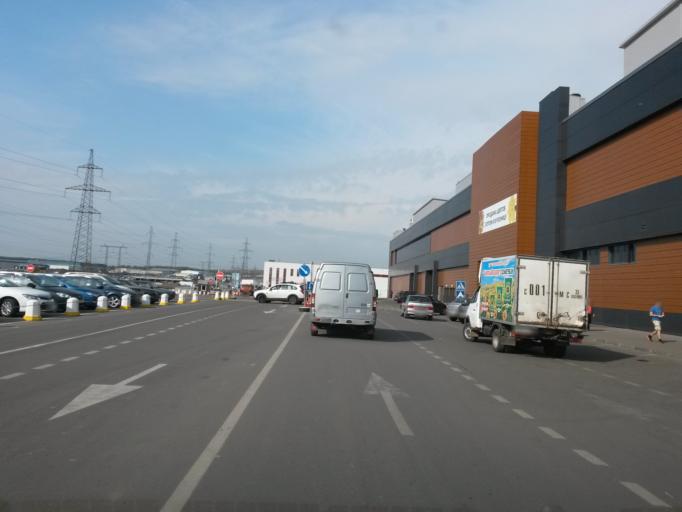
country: RU
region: Moskovskaya
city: Mosrentgen
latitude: 55.6009
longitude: 37.4679
